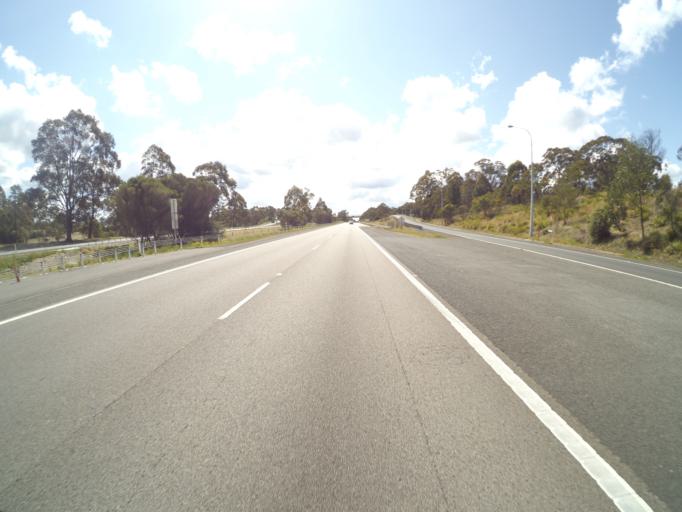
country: AU
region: New South Wales
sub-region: Wingecarribee
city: Colo Vale
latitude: -34.4082
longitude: 150.5041
